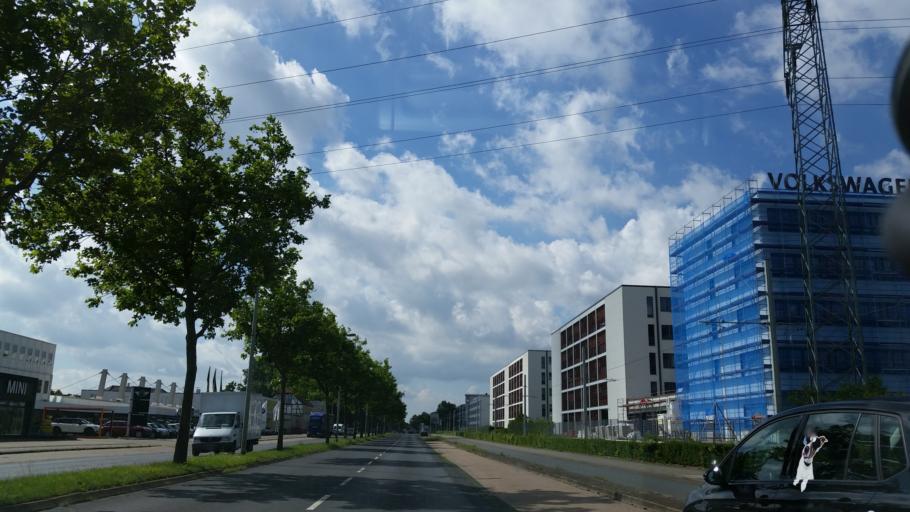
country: DE
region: Lower Saxony
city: Braunschweig
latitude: 52.3013
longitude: 10.5166
